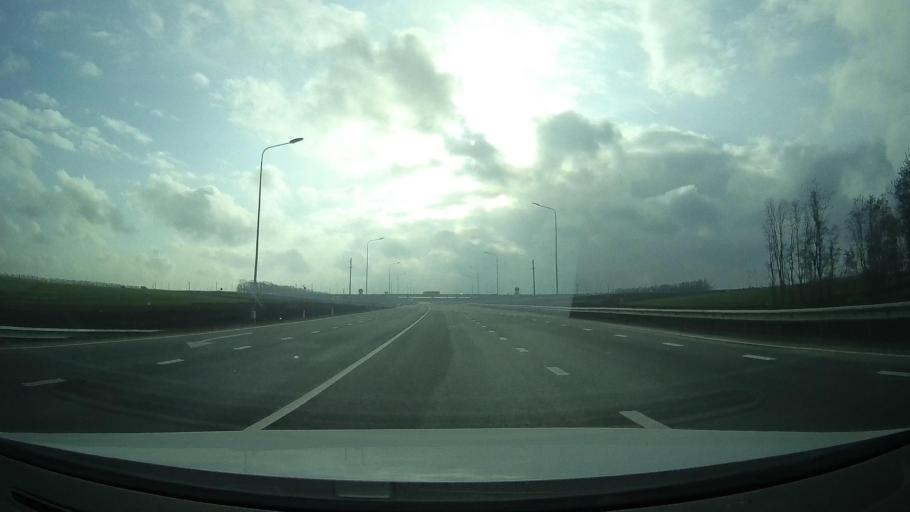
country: RU
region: Rostov
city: Grushevskaya
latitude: 47.3828
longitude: 39.8454
